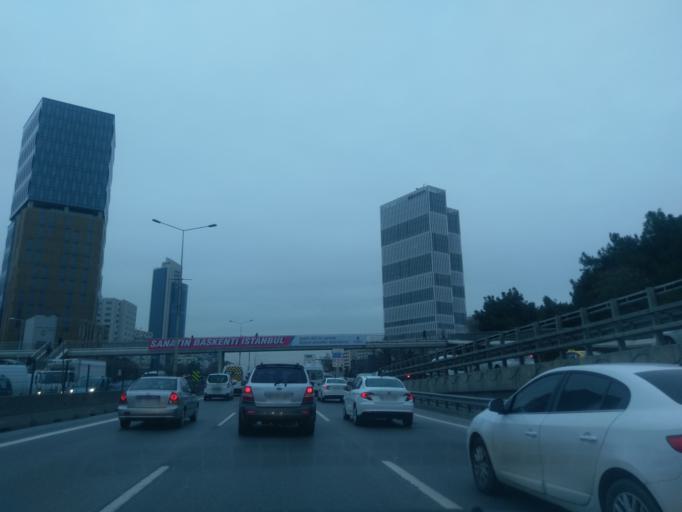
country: TR
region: Istanbul
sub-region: Atasehir
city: Atasehir
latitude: 40.9700
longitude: 29.1021
